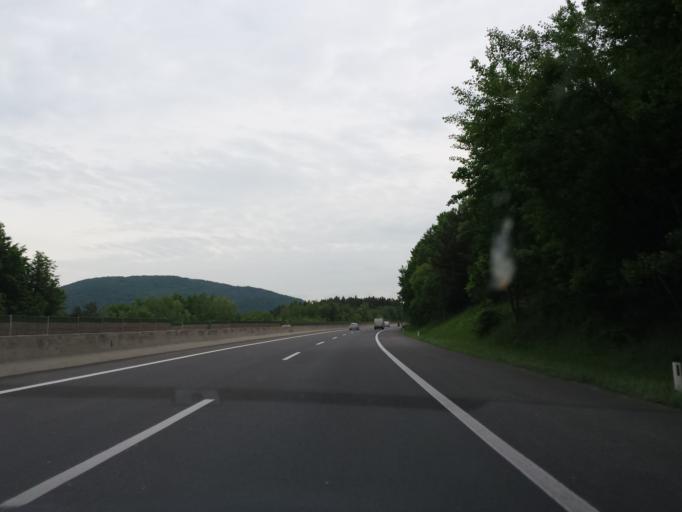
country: AT
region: Lower Austria
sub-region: Politischer Bezirk Neunkirchen
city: Seebenstein
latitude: 47.6710
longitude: 16.1260
